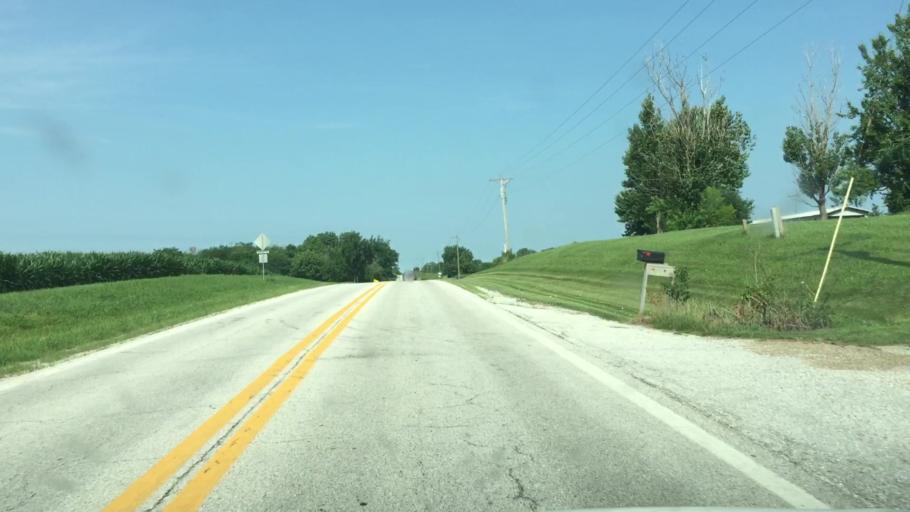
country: US
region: Illinois
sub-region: Hancock County
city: Nauvoo
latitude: 40.5515
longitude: -91.3110
